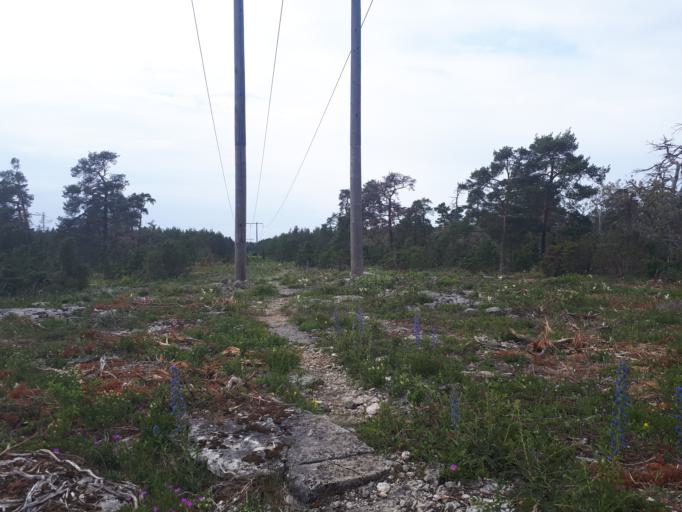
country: SE
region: Gotland
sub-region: Gotland
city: Visby
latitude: 57.6020
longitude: 18.3071
